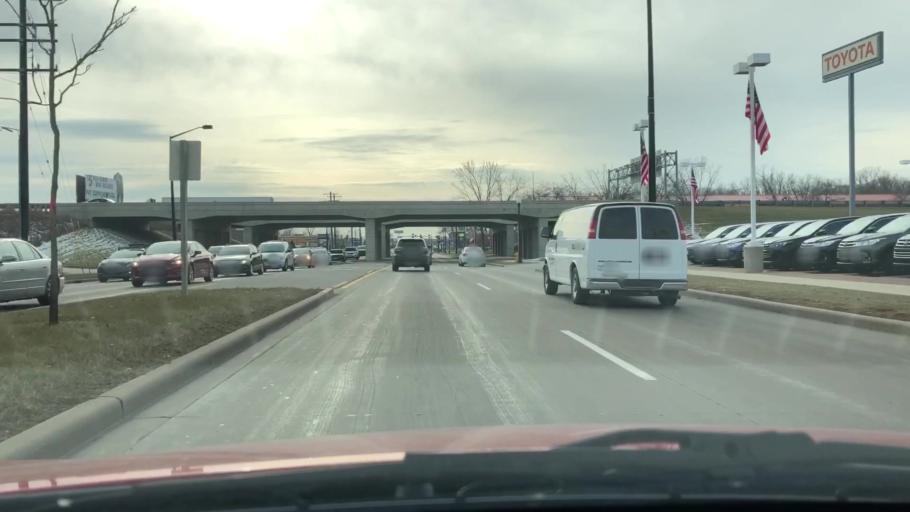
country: US
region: Wisconsin
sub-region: Brown County
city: Ashwaubenon
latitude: 44.4816
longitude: -88.0706
